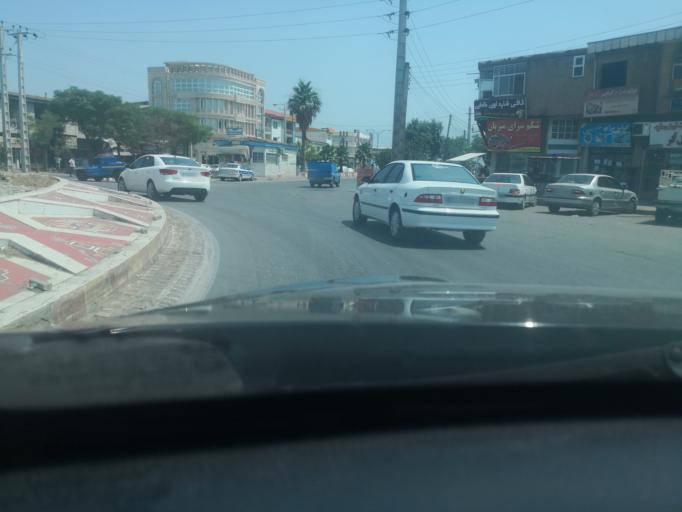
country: IR
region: Golestan
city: Aq Qala
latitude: 37.0093
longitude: 54.4609
